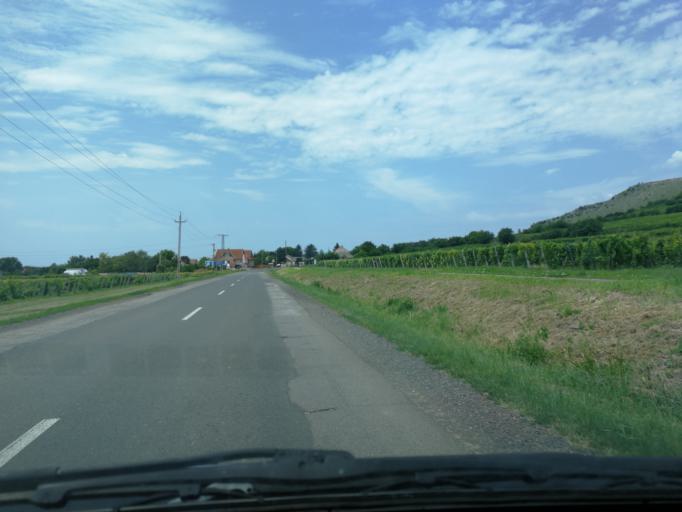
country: HU
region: Baranya
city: Villany
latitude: 45.8478
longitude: 18.4113
